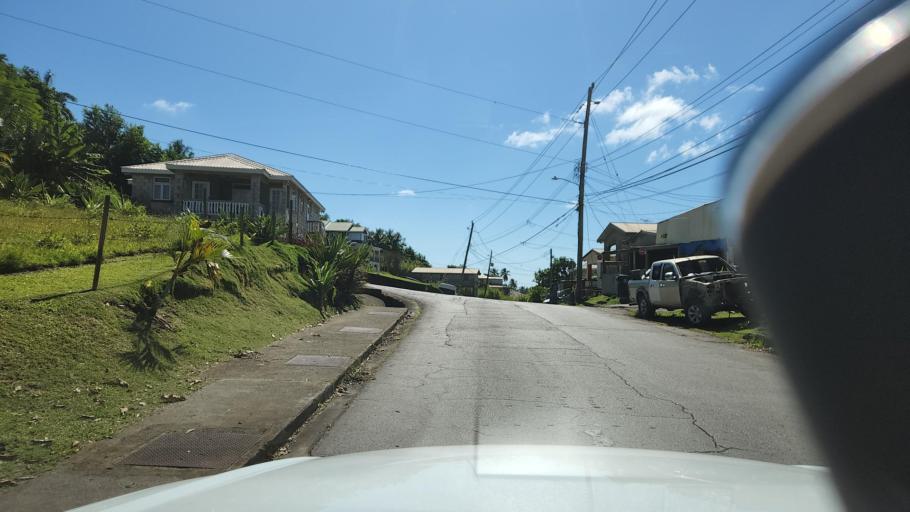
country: BB
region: Saint Thomas
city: Welchman Hall
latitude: 13.1971
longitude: -59.5936
